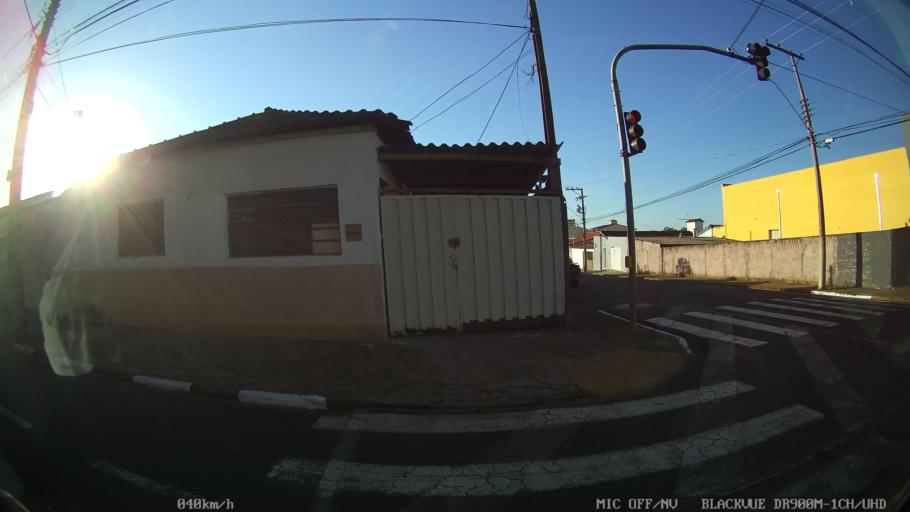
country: BR
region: Sao Paulo
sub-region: Franca
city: Franca
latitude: -20.5255
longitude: -47.3808
